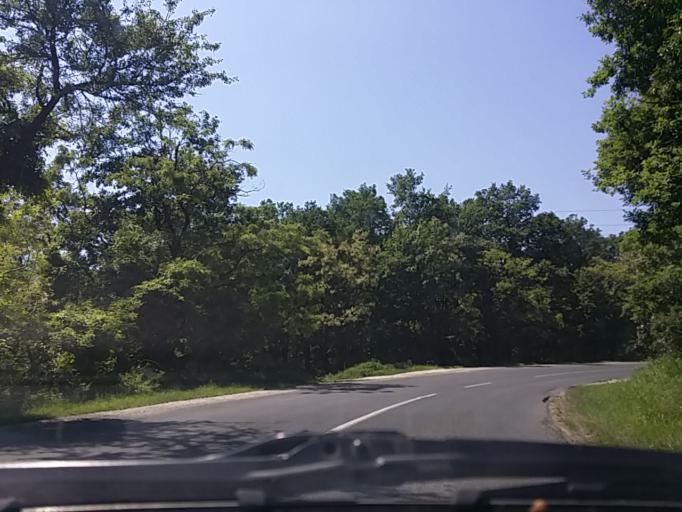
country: HU
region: Pest
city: Pilisszentkereszt
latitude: 47.6999
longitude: 18.8948
